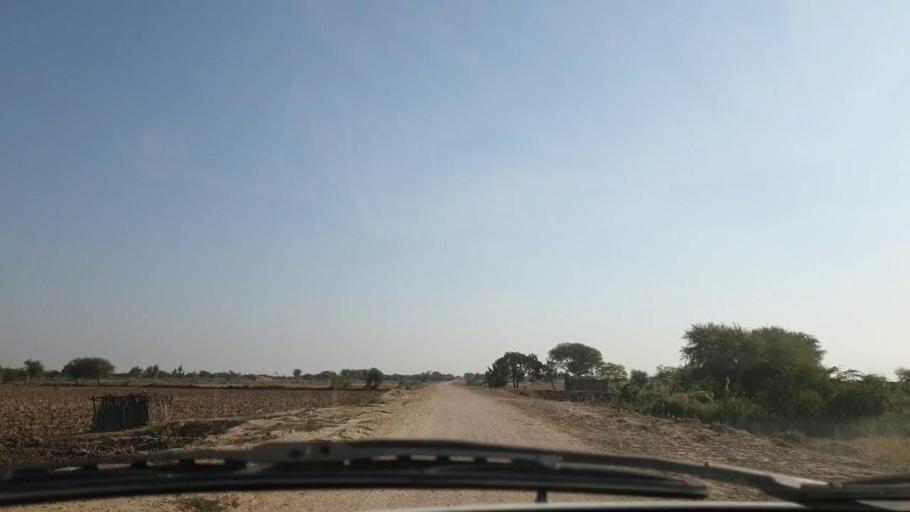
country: PK
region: Sindh
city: Bulri
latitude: 24.8012
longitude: 68.3930
